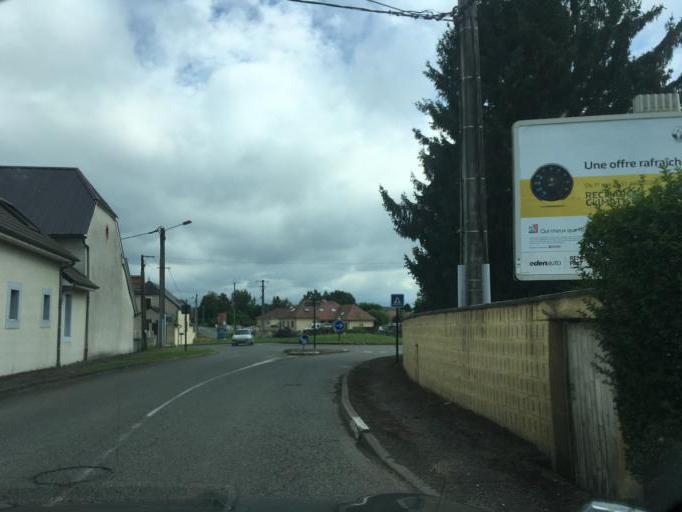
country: FR
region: Aquitaine
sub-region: Departement des Pyrenees-Atlantiques
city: Ousse
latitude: 43.2959
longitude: -0.2722
